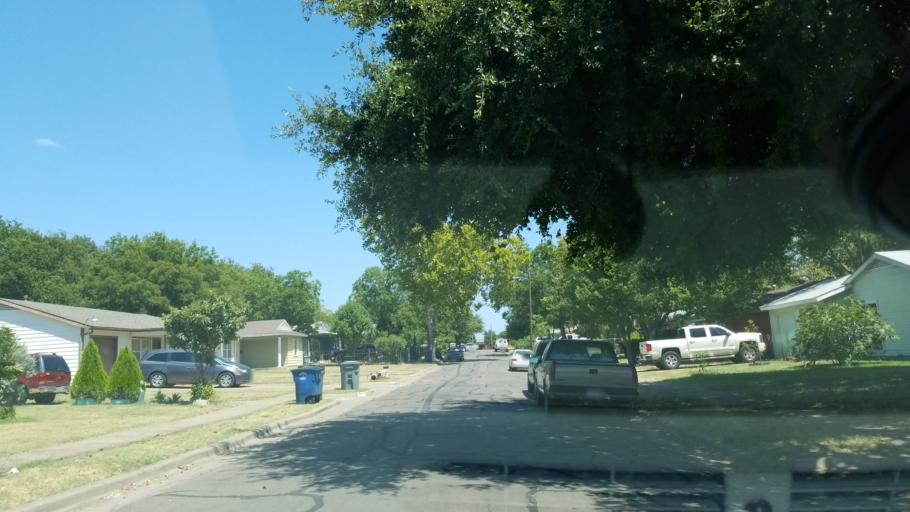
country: US
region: Texas
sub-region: Dallas County
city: Cockrell Hill
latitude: 32.7226
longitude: -96.8845
